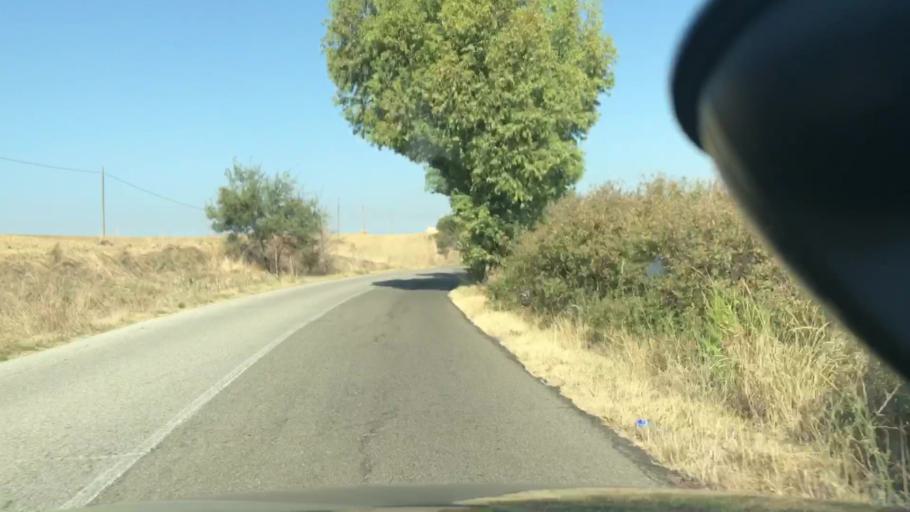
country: IT
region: Basilicate
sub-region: Provincia di Matera
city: La Martella
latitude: 40.6661
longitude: 16.4908
